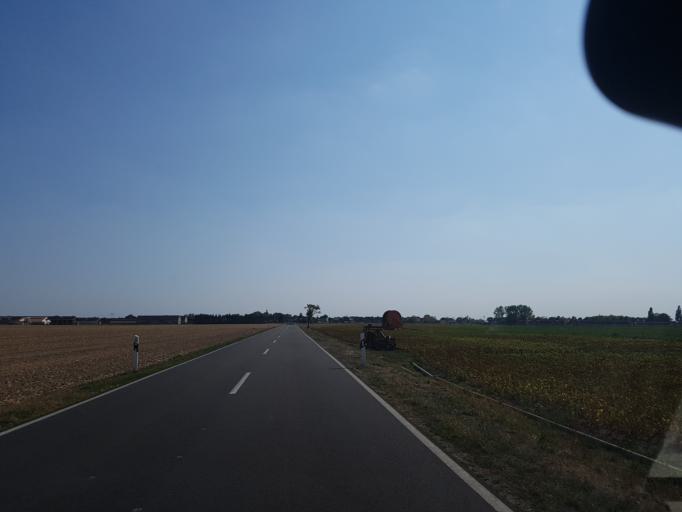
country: DE
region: Saxony-Anhalt
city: Prettin
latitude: 51.6551
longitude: 12.9868
